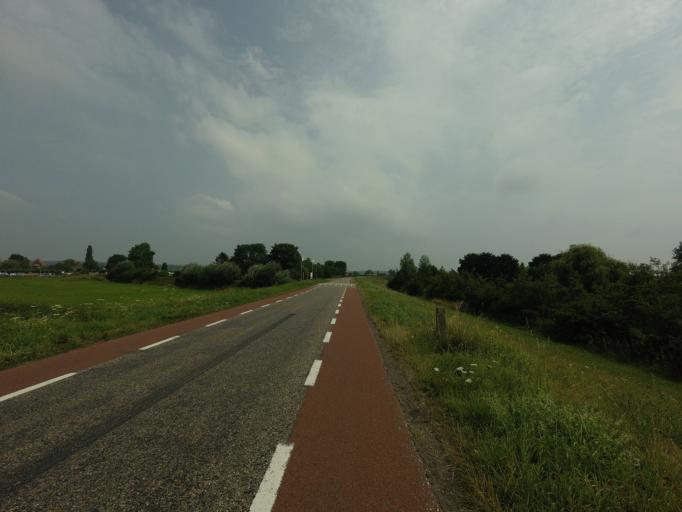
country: NL
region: Utrecht
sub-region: Gemeente Utrechtse Heuvelrug
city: Amerongen
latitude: 51.9800
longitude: 5.4497
